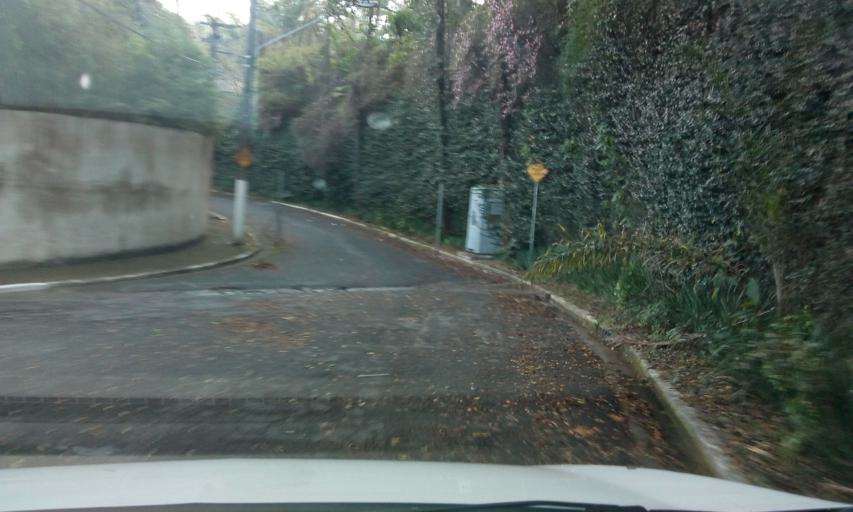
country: BR
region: Sao Paulo
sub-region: Taboao Da Serra
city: Taboao da Serra
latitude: -23.6197
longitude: -46.7047
